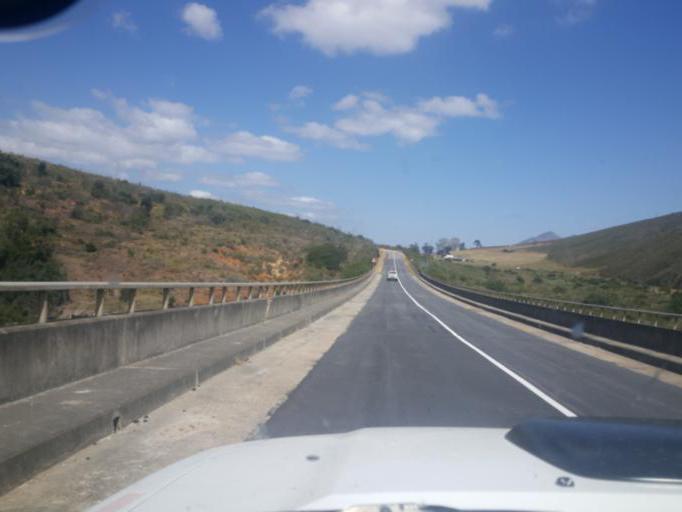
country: ZA
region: Eastern Cape
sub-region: Cacadu District Municipality
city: Kareedouw
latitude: -33.9500
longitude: 24.3401
